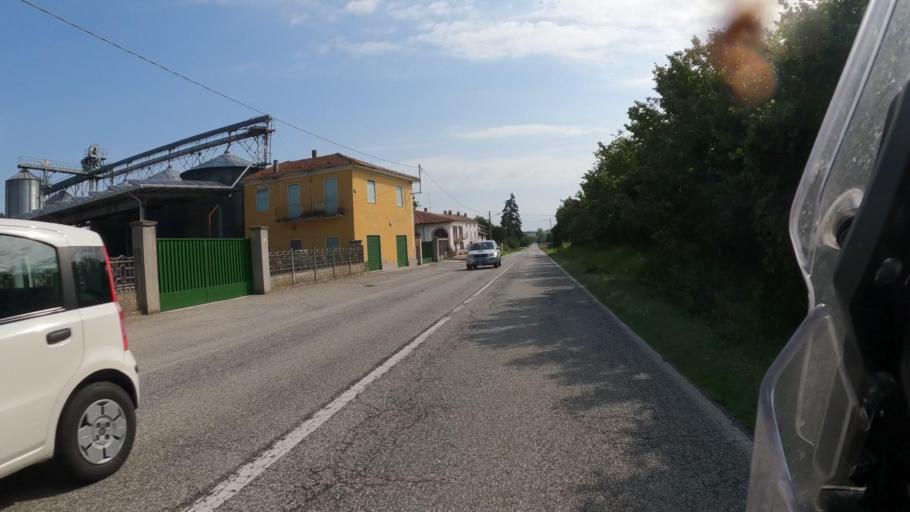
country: IT
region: Piedmont
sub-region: Provincia di Alessandria
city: Vignale Monferrato
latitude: 45.0211
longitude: 8.3961
